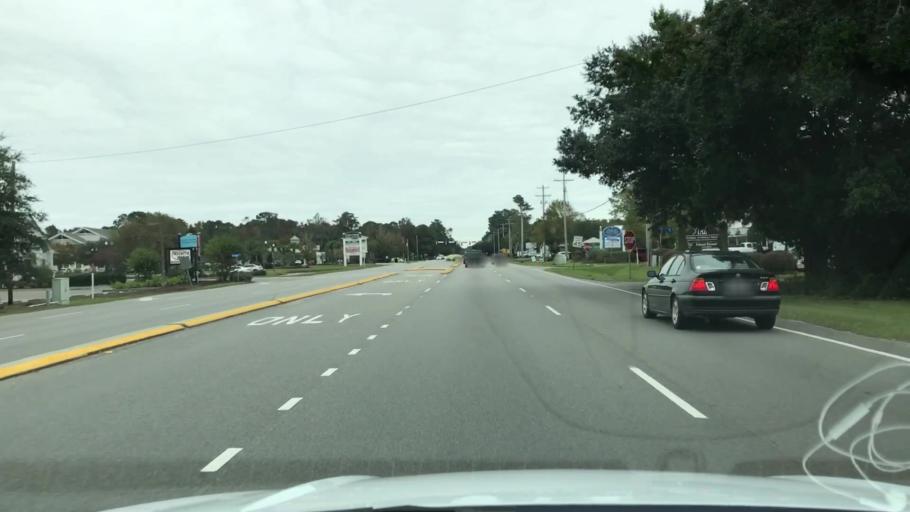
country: US
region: South Carolina
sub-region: Georgetown County
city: Murrells Inlet
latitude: 33.4480
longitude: -79.1206
